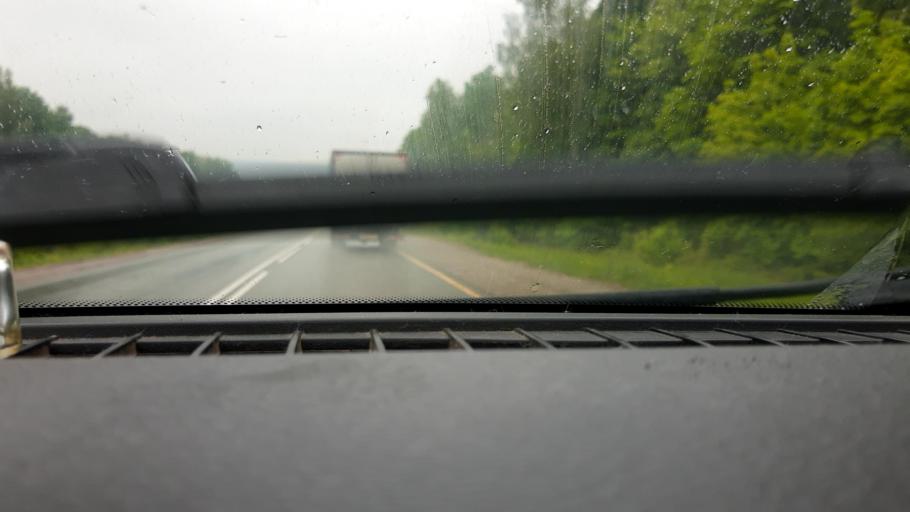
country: RU
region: Bashkortostan
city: Belebey
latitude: 54.2234
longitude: 54.0747
